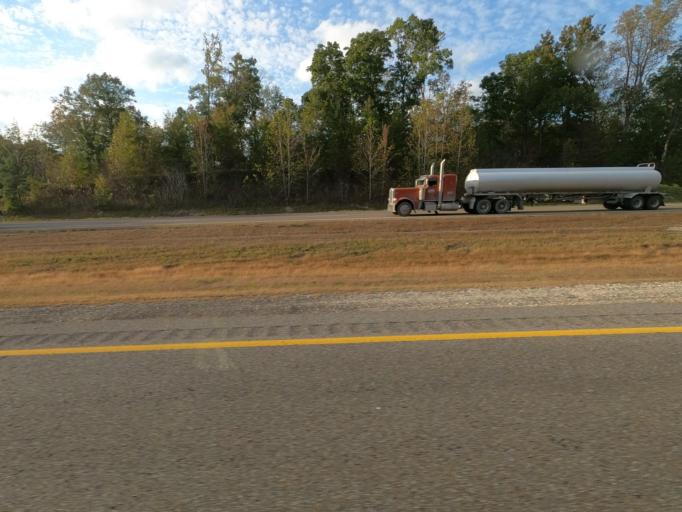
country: US
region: Tennessee
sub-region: Humphreys County
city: New Johnsonville
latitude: 35.8674
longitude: -88.0359
